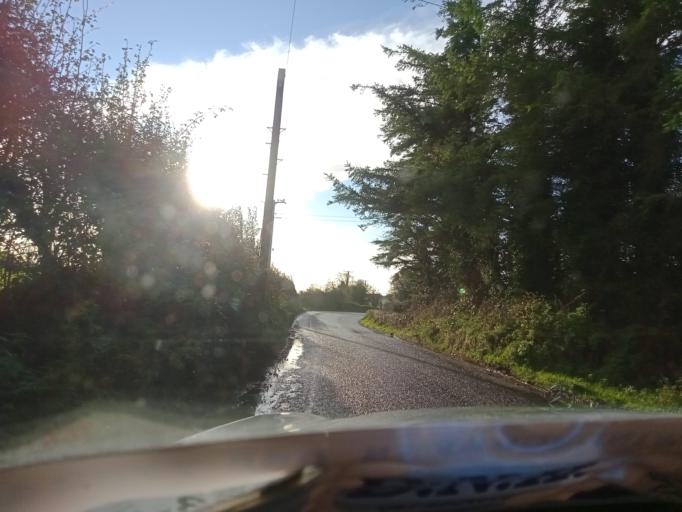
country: IE
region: Leinster
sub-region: Kilkenny
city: Mooncoin
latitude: 52.2786
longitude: -7.2124
